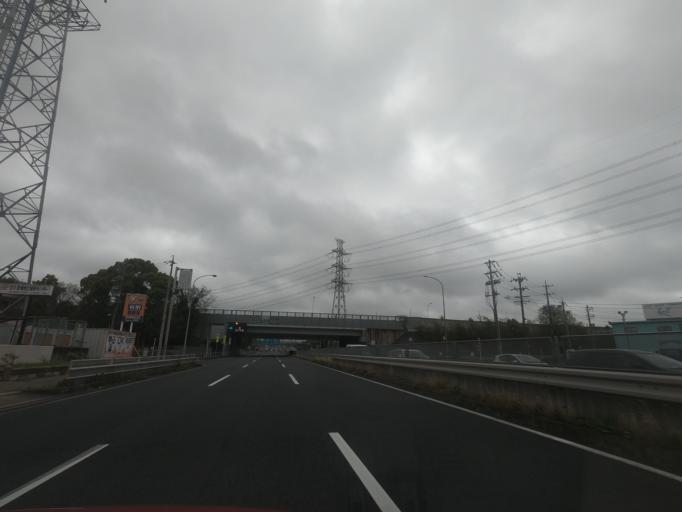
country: JP
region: Aichi
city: Kasugai
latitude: 35.2673
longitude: 136.9948
